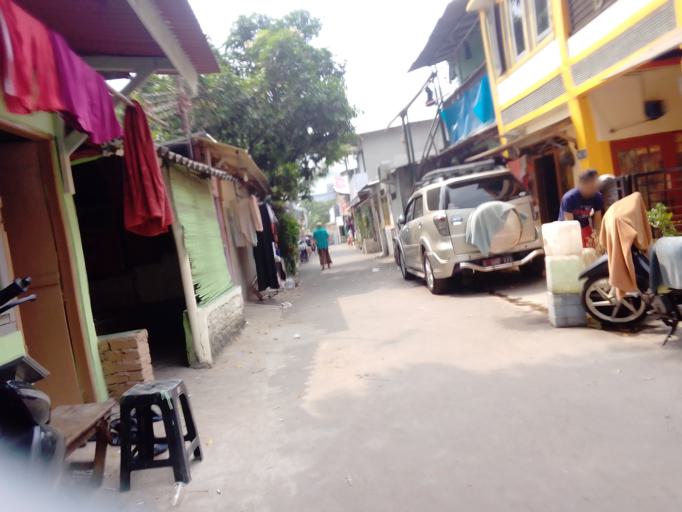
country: ID
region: Jakarta Raya
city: Jakarta
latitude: -6.2012
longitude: 106.8187
